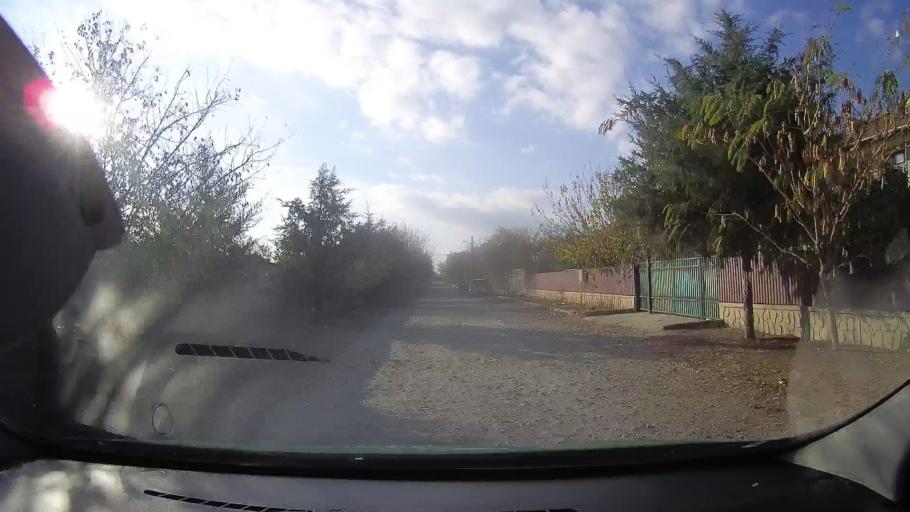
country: RO
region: Constanta
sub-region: Comuna Lumina
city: Lumina
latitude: 44.2876
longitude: 28.5594
